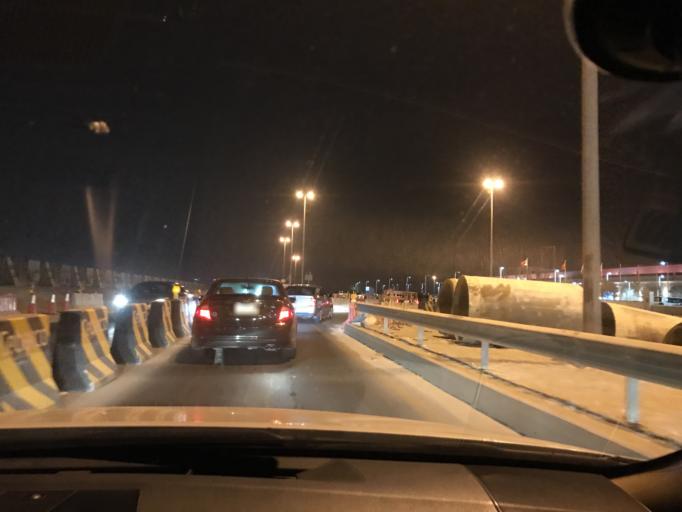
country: BH
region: Muharraq
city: Al Muharraq
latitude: 26.3055
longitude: 50.6281
